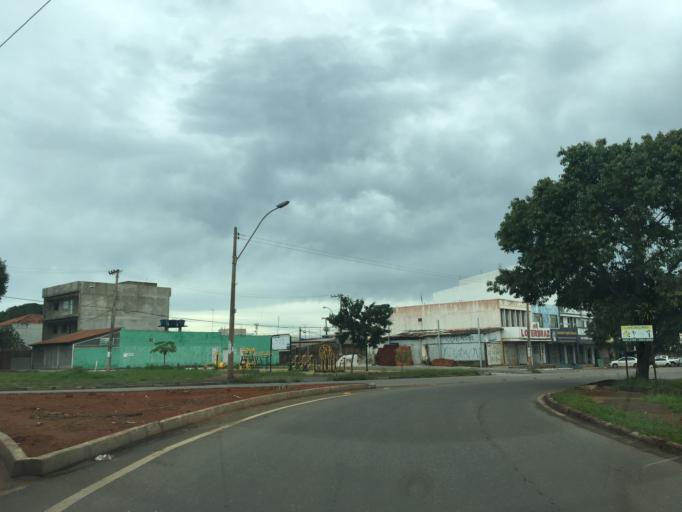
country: BR
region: Goias
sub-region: Luziania
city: Luziania
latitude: -16.0235
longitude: -48.0607
